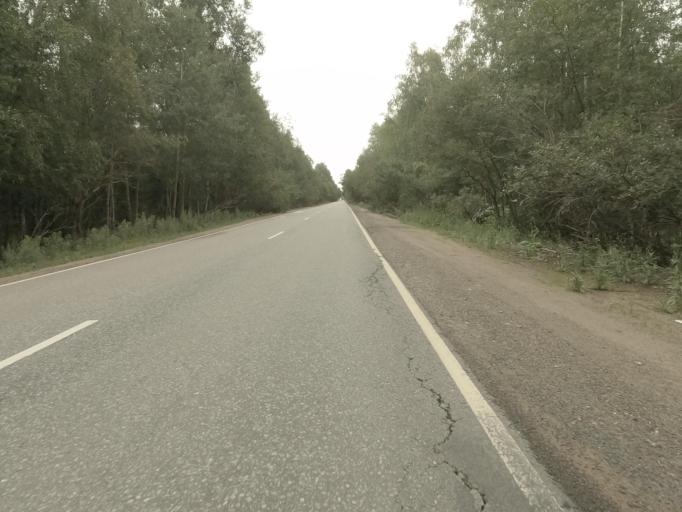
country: RU
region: Leningrad
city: Koltushi
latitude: 59.8998
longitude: 30.7651
